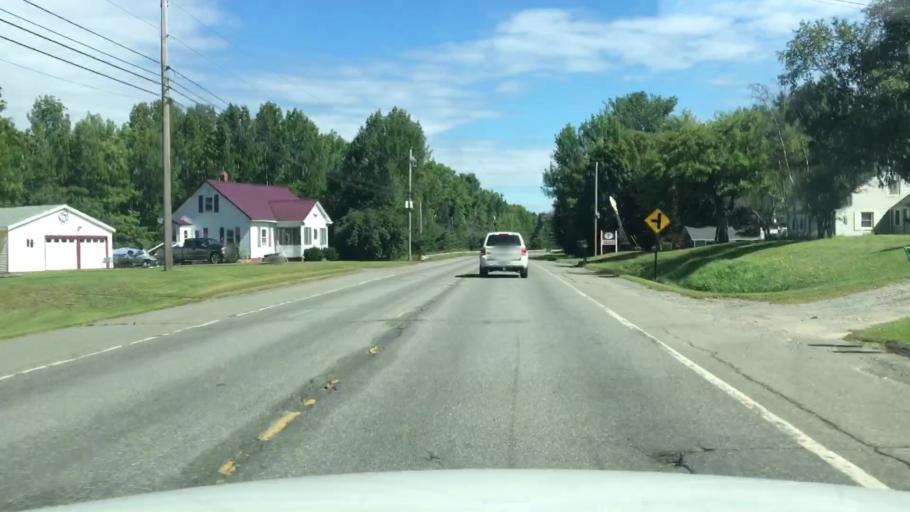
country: US
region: Maine
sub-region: Penobscot County
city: Dexter
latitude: 45.0456
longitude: -69.2720
